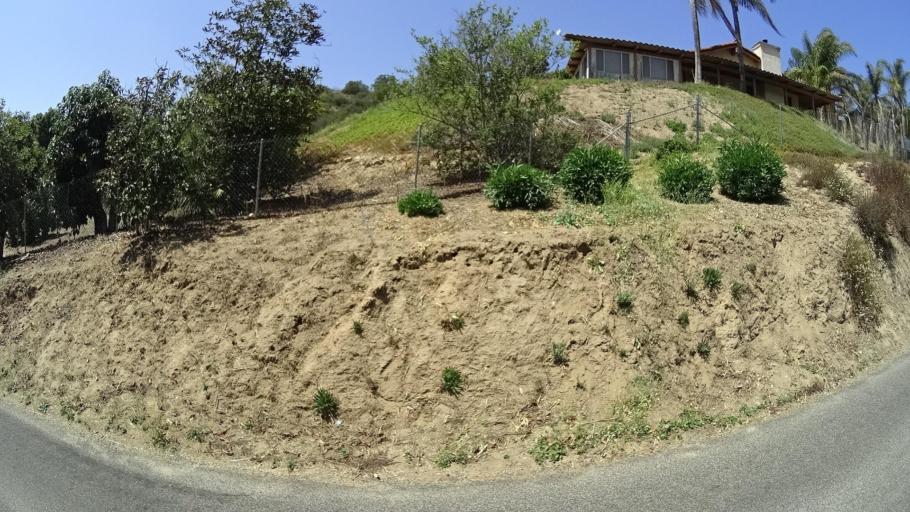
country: US
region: California
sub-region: San Diego County
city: Fallbrook
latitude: 33.4455
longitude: -117.2856
